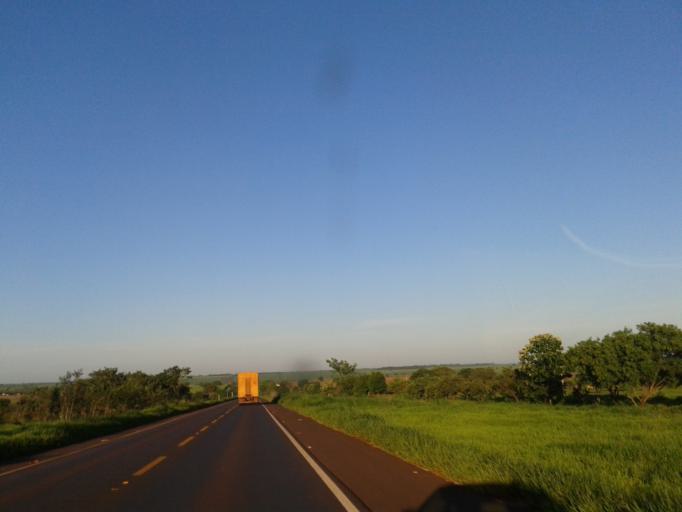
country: BR
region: Minas Gerais
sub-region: Ituiutaba
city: Ituiutaba
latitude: -18.9655
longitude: -49.5056
